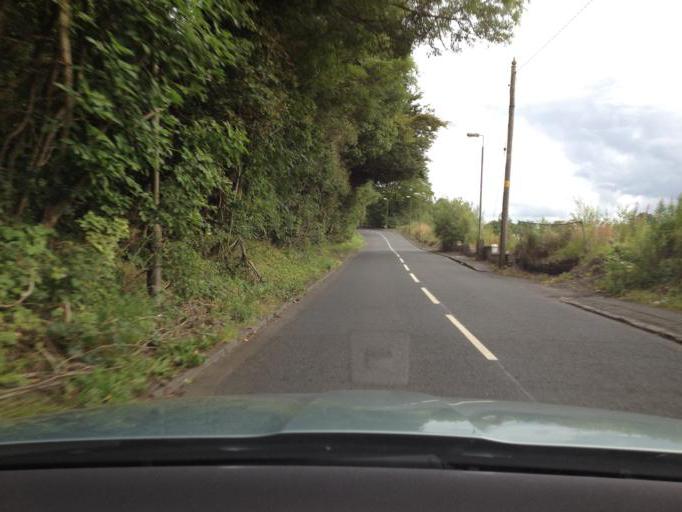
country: GB
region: Scotland
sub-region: West Lothian
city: Armadale
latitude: 55.9322
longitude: -3.6953
